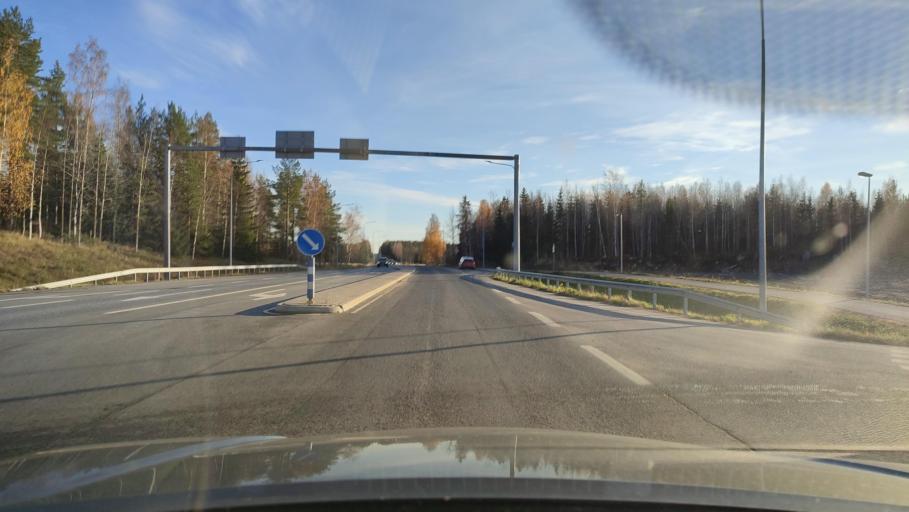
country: FI
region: Ostrobothnia
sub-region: Vaasa
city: Ristinummi
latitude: 63.0244
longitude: 21.7565
